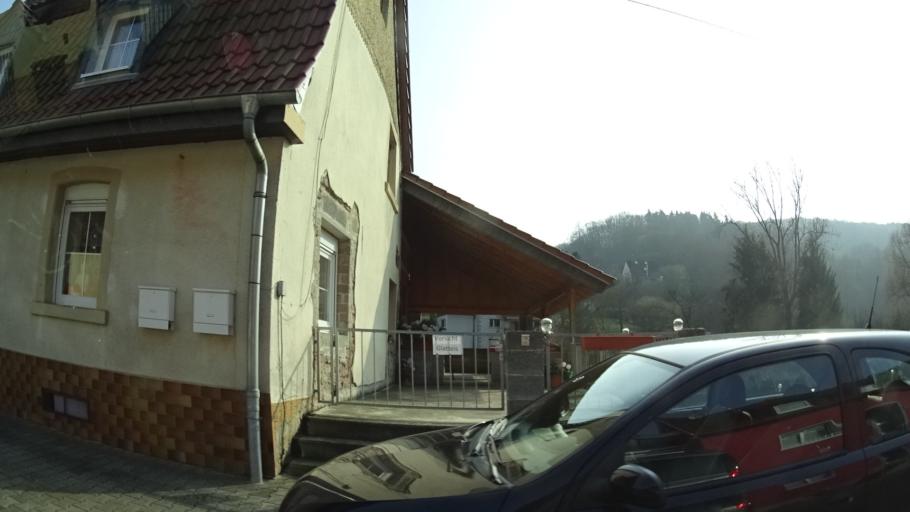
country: DE
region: Rheinland-Pfalz
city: Fockelberg
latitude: 49.5438
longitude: 7.4951
